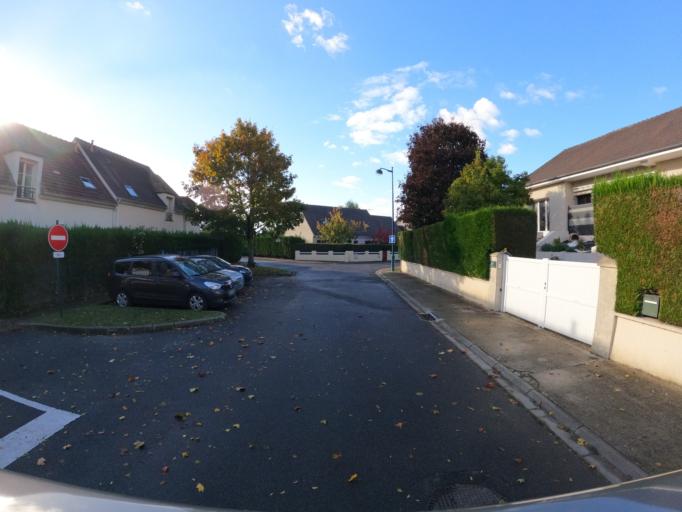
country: FR
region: Ile-de-France
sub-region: Departement de Seine-et-Marne
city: Bailly-Romainvilliers
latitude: 48.8483
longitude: 2.8268
